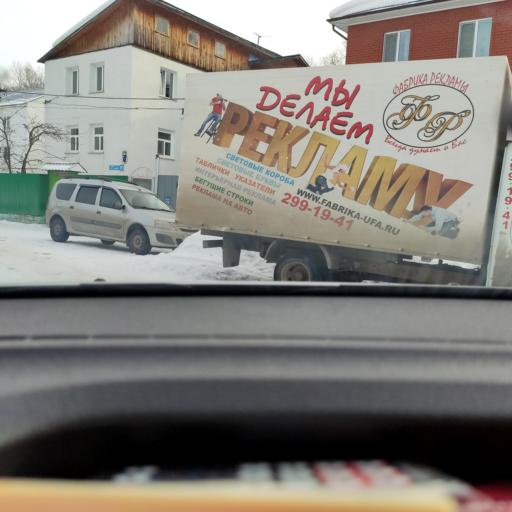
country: RU
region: Bashkortostan
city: Ufa
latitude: 54.7099
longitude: 55.9291
